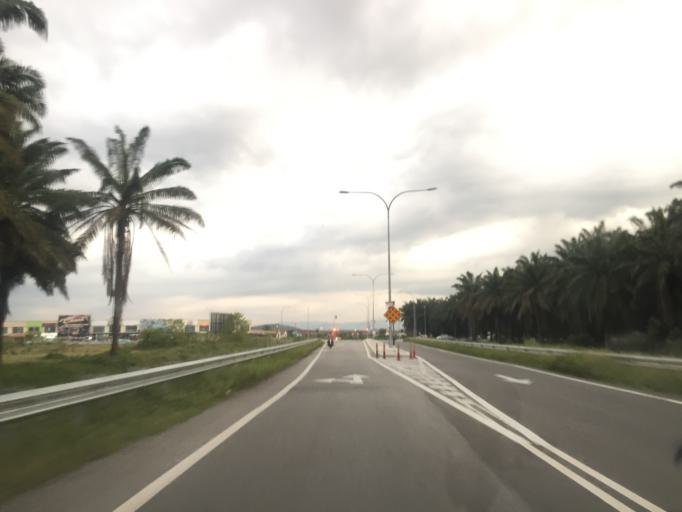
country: MY
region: Penang
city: Tasek Glugor
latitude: 5.5139
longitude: 100.5319
